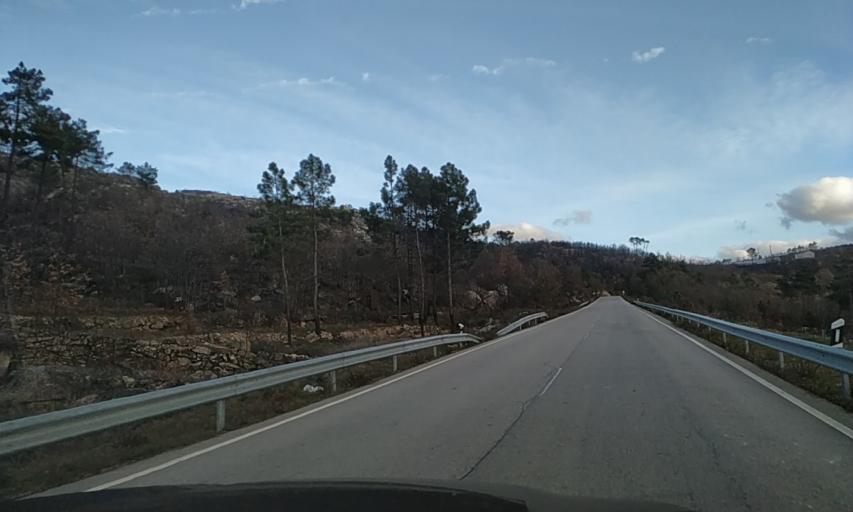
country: PT
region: Braganca
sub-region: Carrazeda de Ansiaes
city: Carrazeda de Anciaes
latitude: 41.2579
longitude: -7.3194
